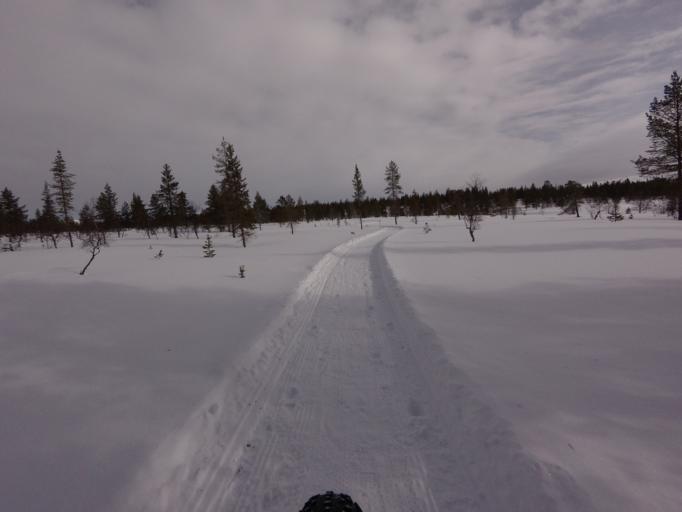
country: FI
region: Lapland
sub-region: Pohjois-Lappi
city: Ivalo
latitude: 68.3473
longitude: 27.4506
